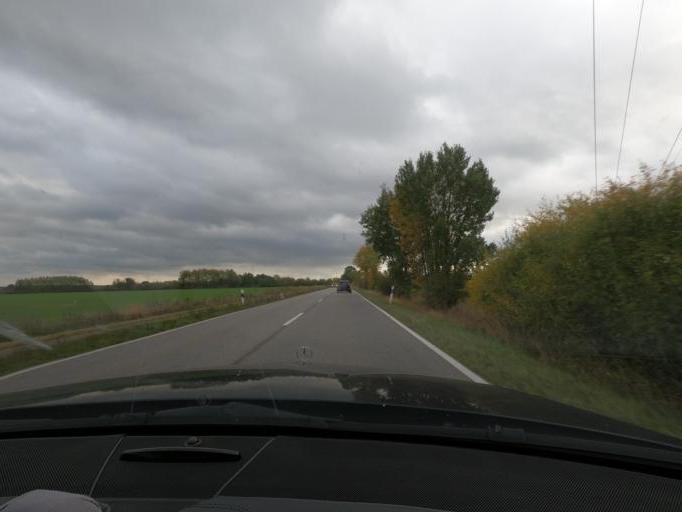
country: DE
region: Schleswig-Holstein
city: Hohenhorn
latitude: 53.4614
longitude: 10.3688
